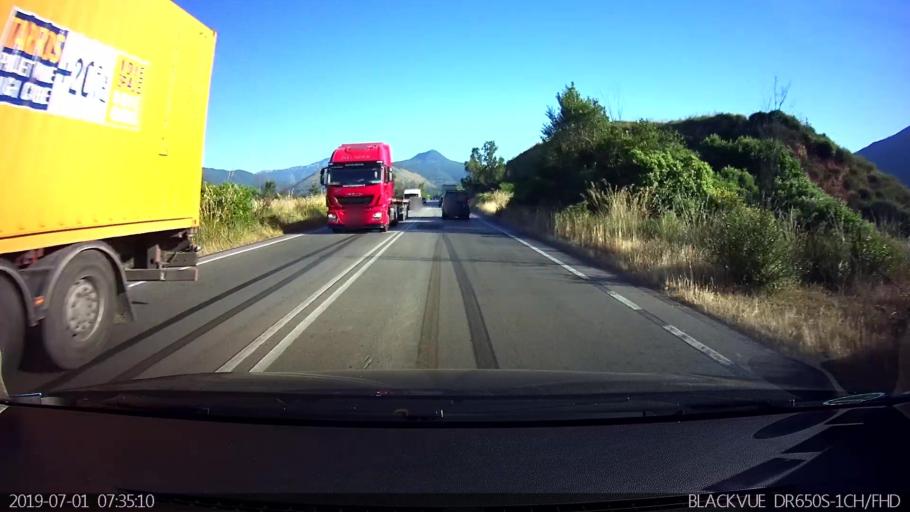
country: IT
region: Latium
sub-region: Provincia di Latina
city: Prossedi
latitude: 41.5225
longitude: 13.2716
